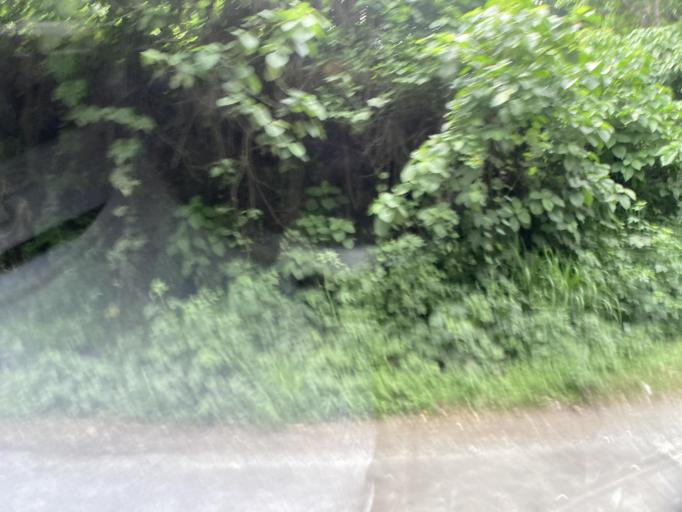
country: GT
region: Guatemala
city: Villa Canales
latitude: 14.4409
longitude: -90.5339
